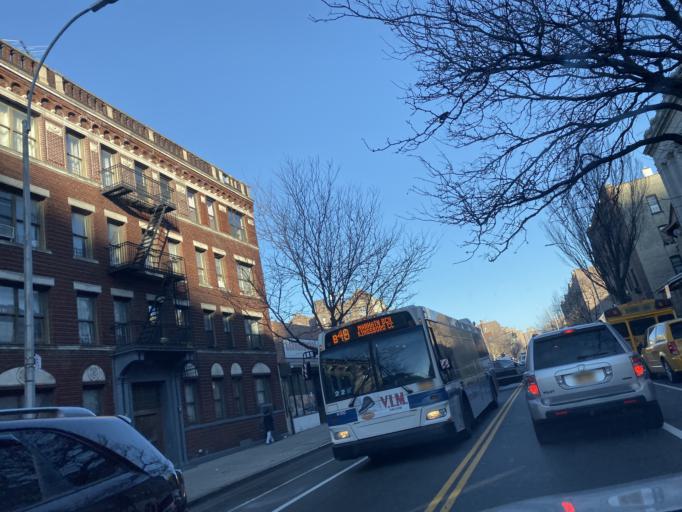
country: US
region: New York
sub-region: Kings County
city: Brooklyn
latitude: 40.6542
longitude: -73.9562
